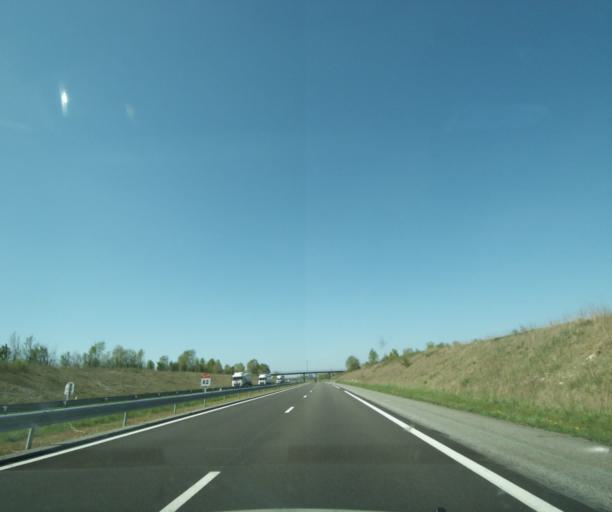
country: FR
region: Bourgogne
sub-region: Departement de la Nievre
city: Neuvy-sur-Loire
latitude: 47.5633
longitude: 2.8812
